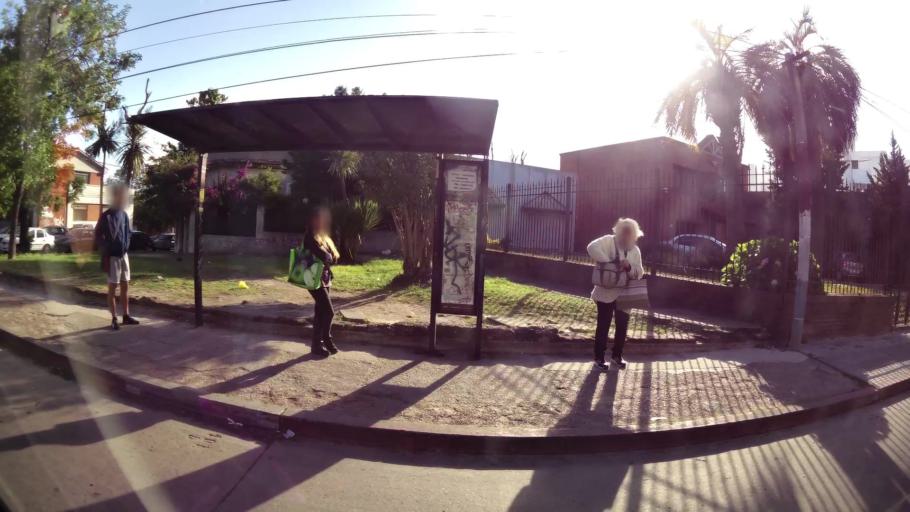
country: UY
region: Montevideo
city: Montevideo
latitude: -34.8769
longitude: -56.1571
